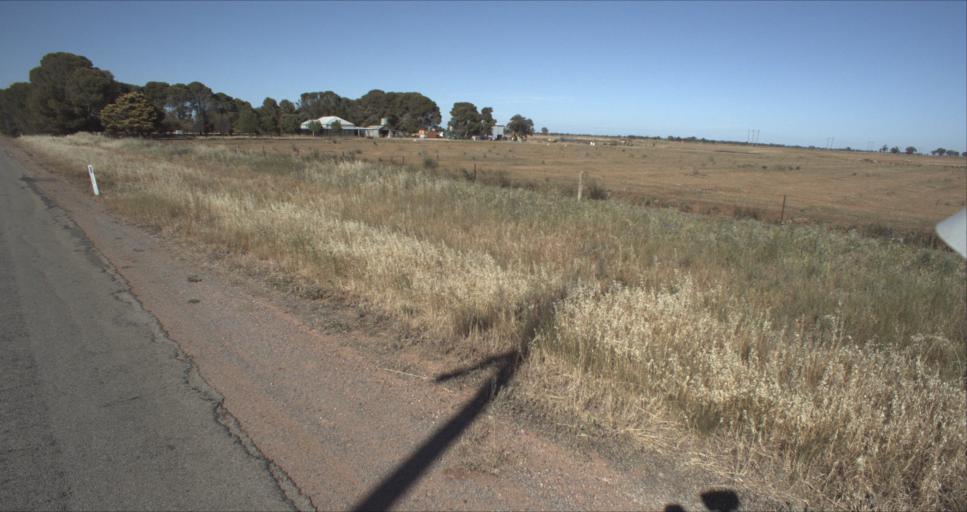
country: AU
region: New South Wales
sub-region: Leeton
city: Leeton
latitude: -34.5707
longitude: 146.3107
